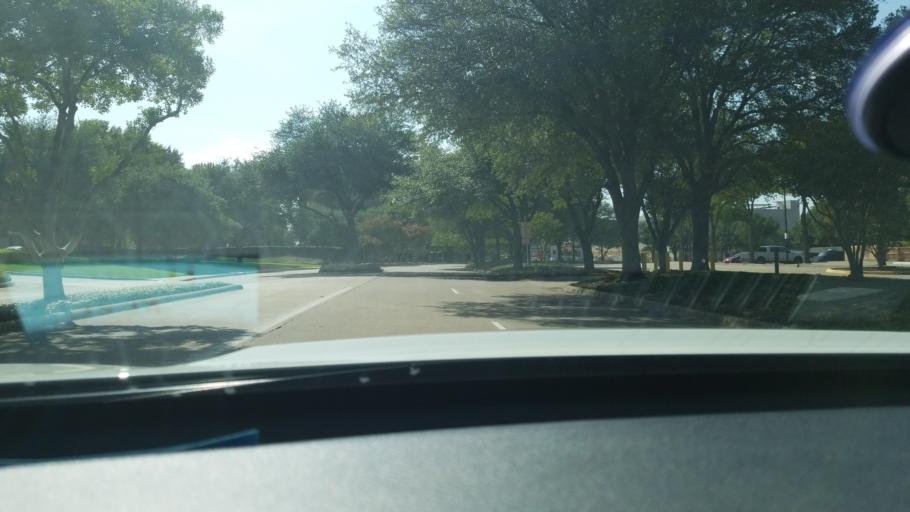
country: US
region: Texas
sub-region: Dallas County
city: Addison
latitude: 32.9557
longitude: -96.8230
